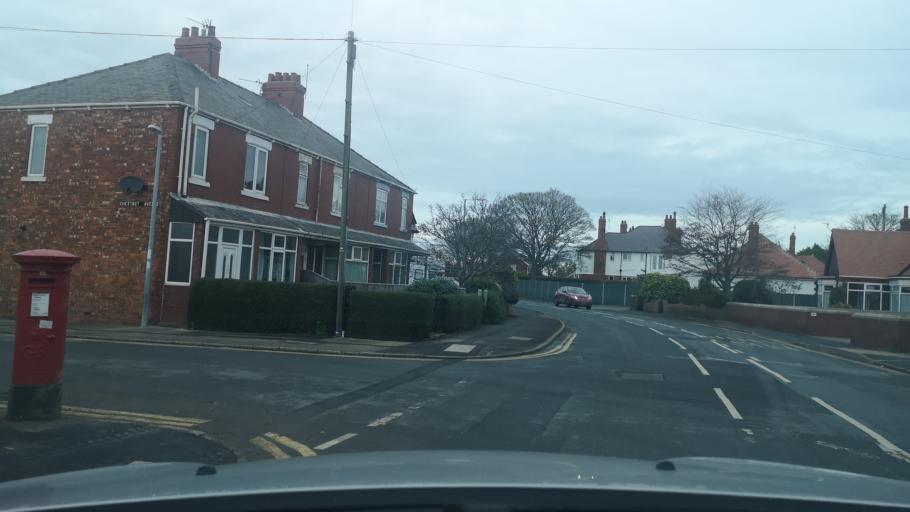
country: GB
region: England
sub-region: East Riding of Yorkshire
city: Withernsea
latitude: 53.7216
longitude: 0.0394
